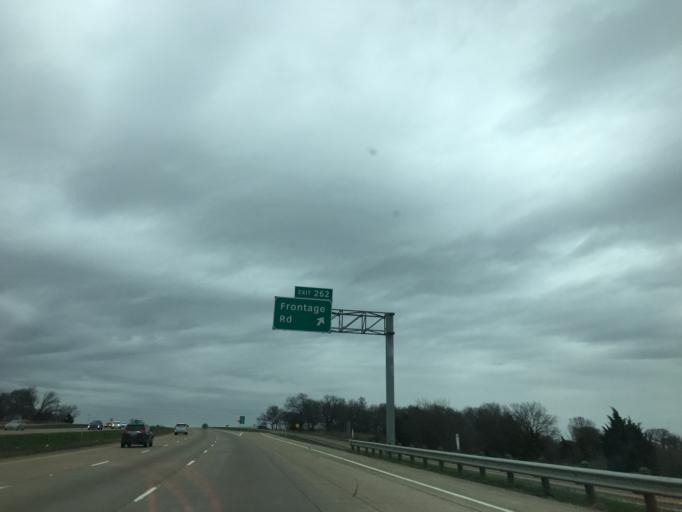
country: US
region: Texas
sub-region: Ellis County
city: Palmer
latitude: 32.4723
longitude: -96.6608
